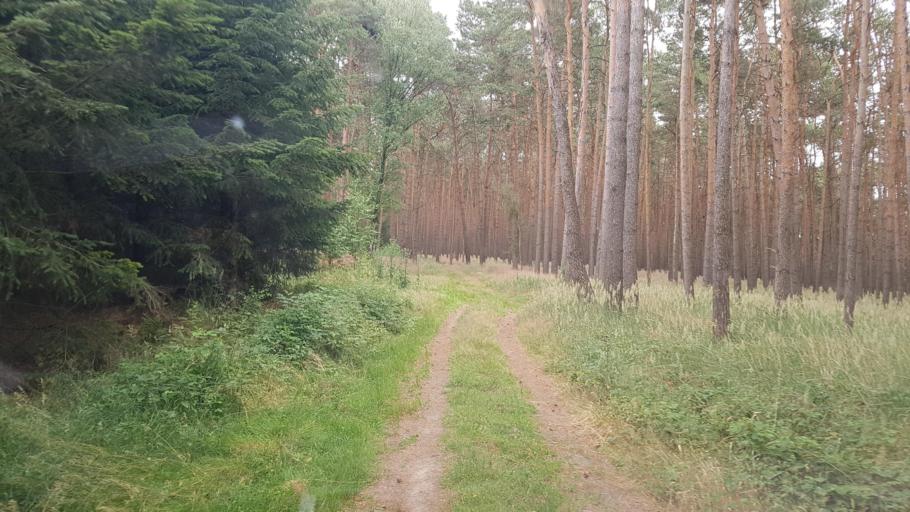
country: DE
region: Brandenburg
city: Treuenbrietzen
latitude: 52.0370
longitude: 12.8359
